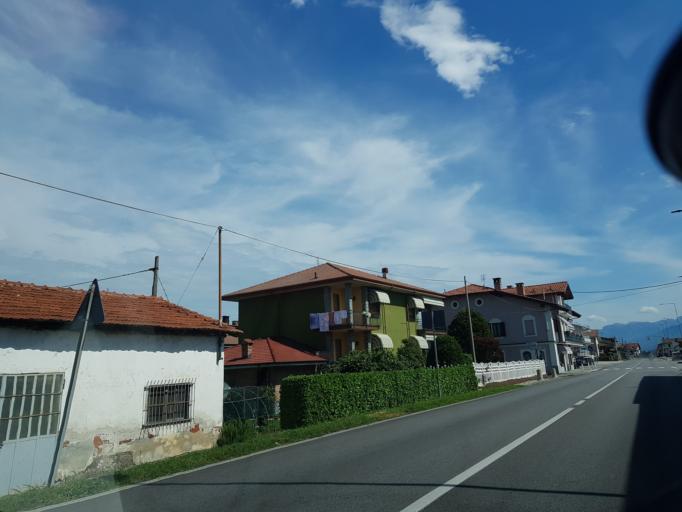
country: IT
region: Piedmont
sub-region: Provincia di Cuneo
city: Tarantasca
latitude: 44.4815
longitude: 7.5044
